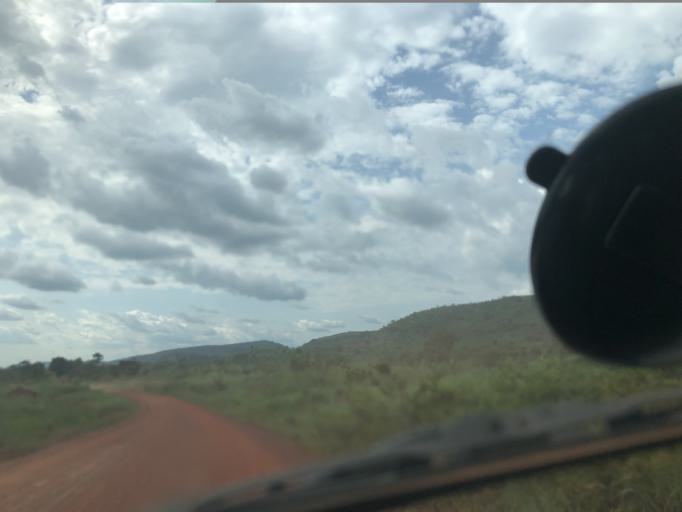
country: CF
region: Bangui
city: Bangui
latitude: 4.2829
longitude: 18.6230
